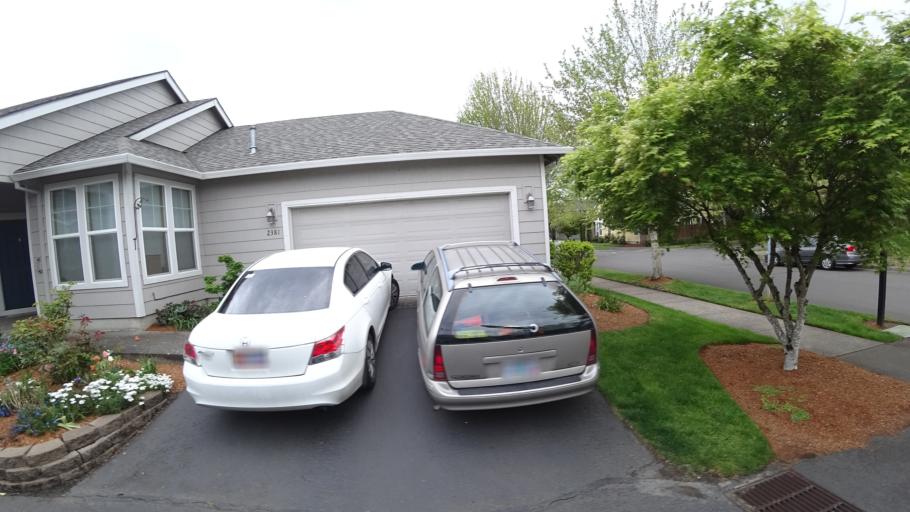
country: US
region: Oregon
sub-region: Washington County
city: Hillsboro
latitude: 45.5418
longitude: -122.9679
